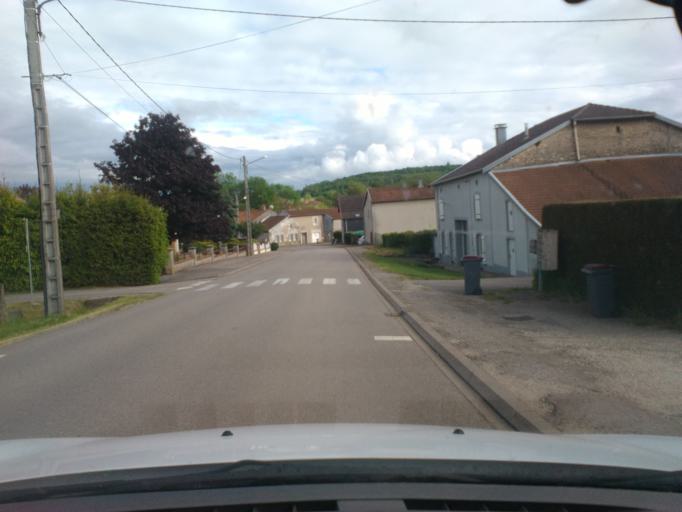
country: FR
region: Lorraine
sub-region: Departement des Vosges
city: Mirecourt
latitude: 48.3146
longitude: 6.0513
